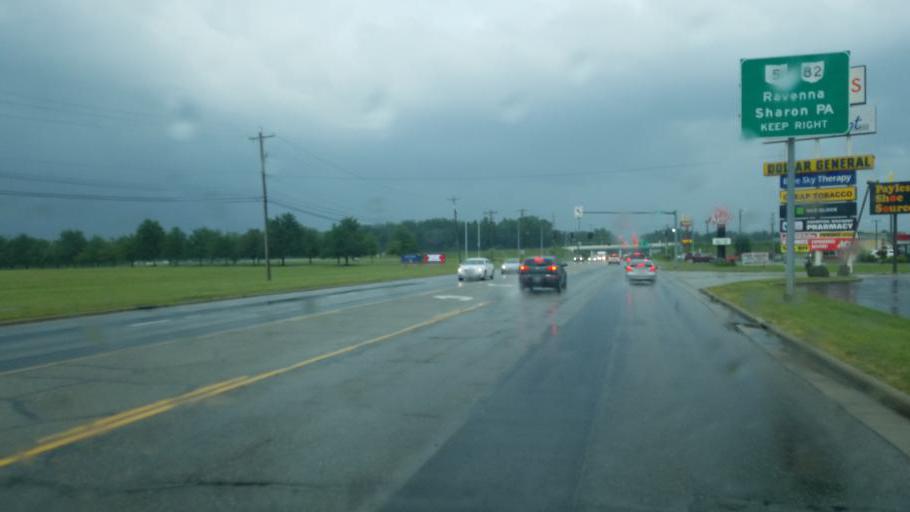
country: US
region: Ohio
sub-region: Trumbull County
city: Champion Heights
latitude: 41.2788
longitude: -80.8432
